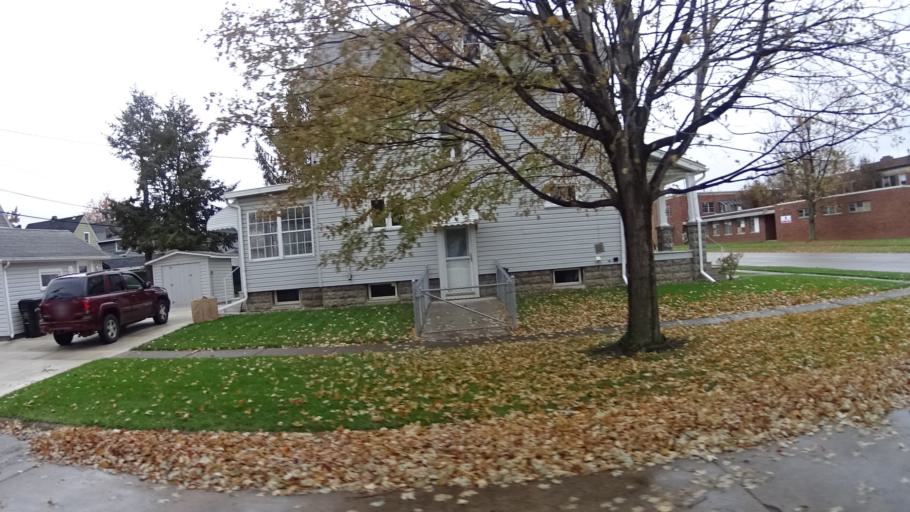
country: US
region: Ohio
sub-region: Lorain County
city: Elyria
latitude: 41.3782
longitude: -82.1186
